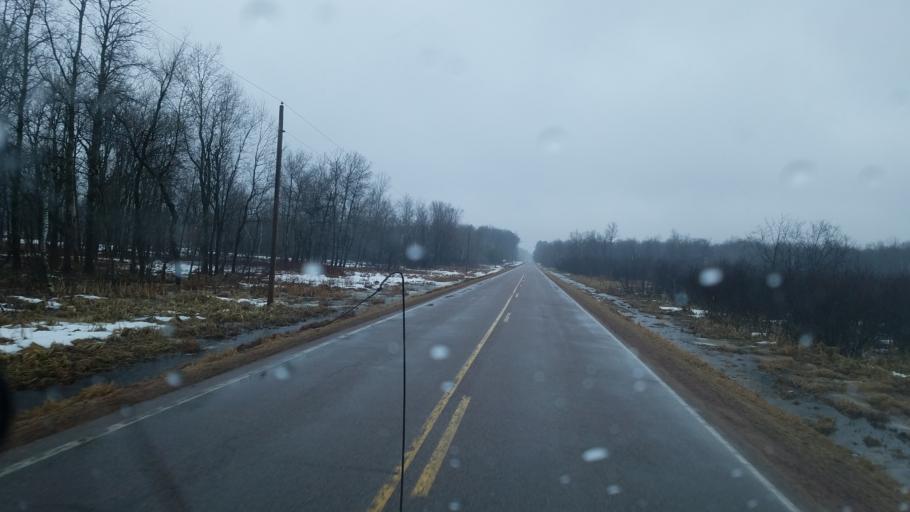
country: US
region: Wisconsin
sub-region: Wood County
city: Marshfield
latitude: 44.4546
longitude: -90.2797
